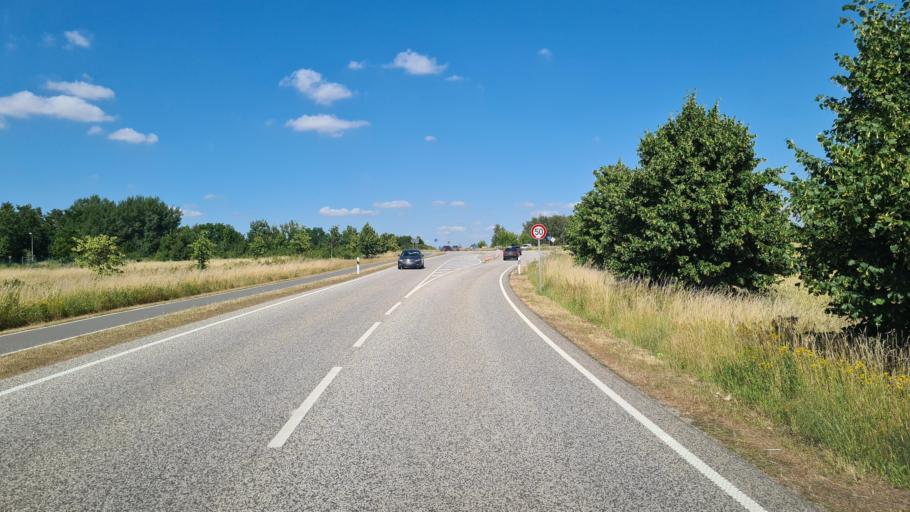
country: DE
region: Saxony-Anhalt
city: Abtsdorf
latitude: 51.8787
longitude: 12.6792
